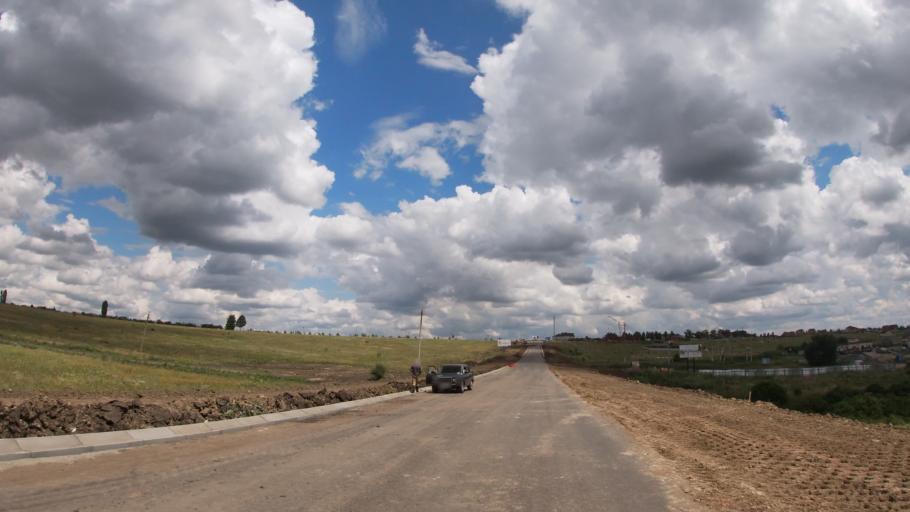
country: RU
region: Belgorod
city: Mayskiy
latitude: 50.5239
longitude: 36.5121
